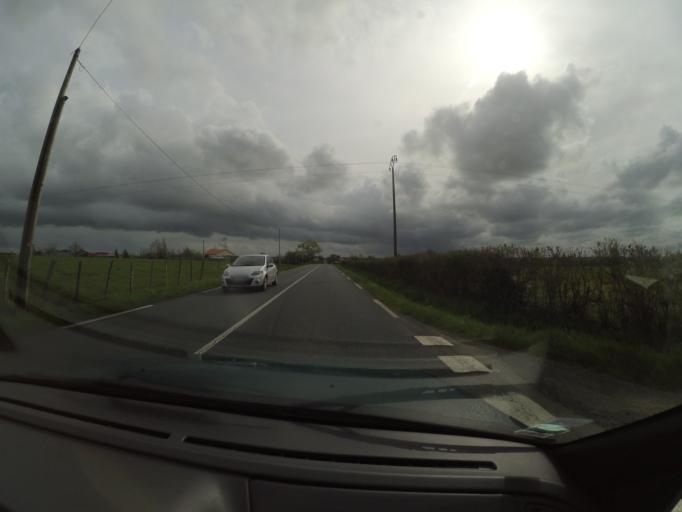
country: FR
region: Pays de la Loire
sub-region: Departement de la Loire-Atlantique
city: La Remaudiere
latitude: 47.2463
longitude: -1.2102
